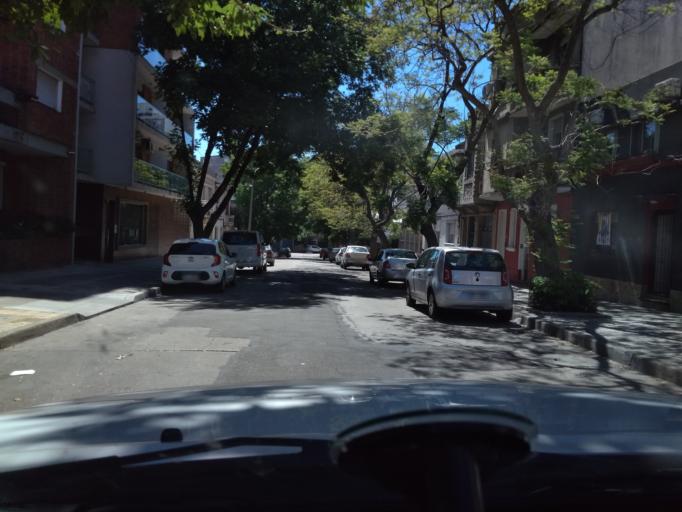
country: UY
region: Montevideo
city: Montevideo
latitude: -34.9069
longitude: -56.1530
